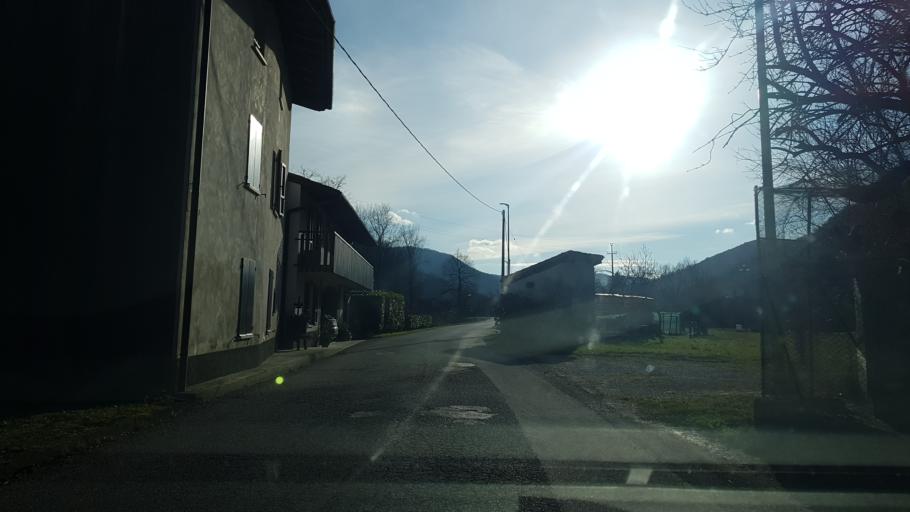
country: IT
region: Friuli Venezia Giulia
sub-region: Provincia di Udine
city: Merso di Sopra
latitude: 46.1362
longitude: 13.5380
